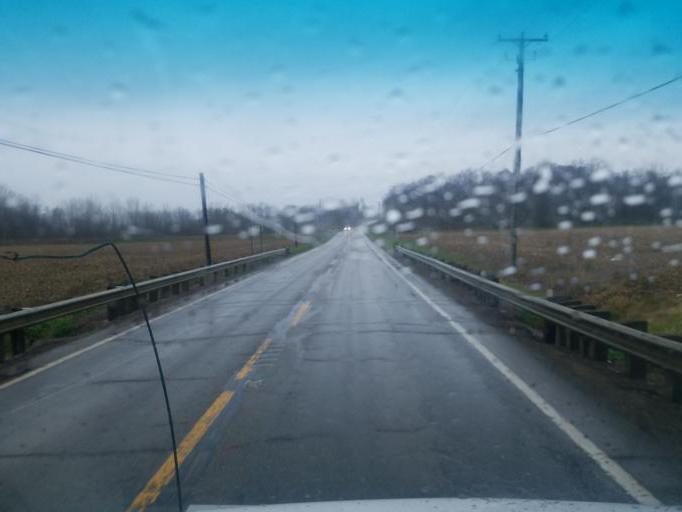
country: US
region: Ohio
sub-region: Holmes County
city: Millersburg
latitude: 40.6134
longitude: -81.9158
